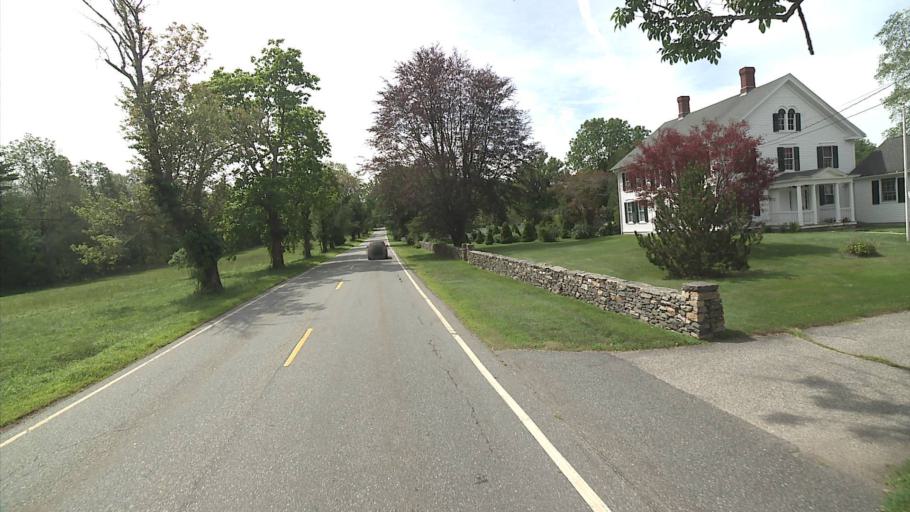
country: US
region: Connecticut
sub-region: Windham County
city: Putnam
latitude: 41.8951
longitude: -71.8670
